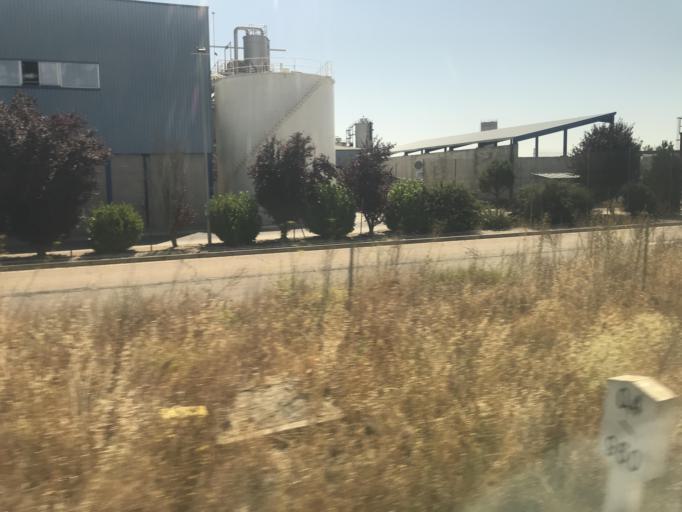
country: ES
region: Castille and Leon
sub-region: Provincia de Palencia
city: Duenas
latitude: 41.8403
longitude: -4.5599
